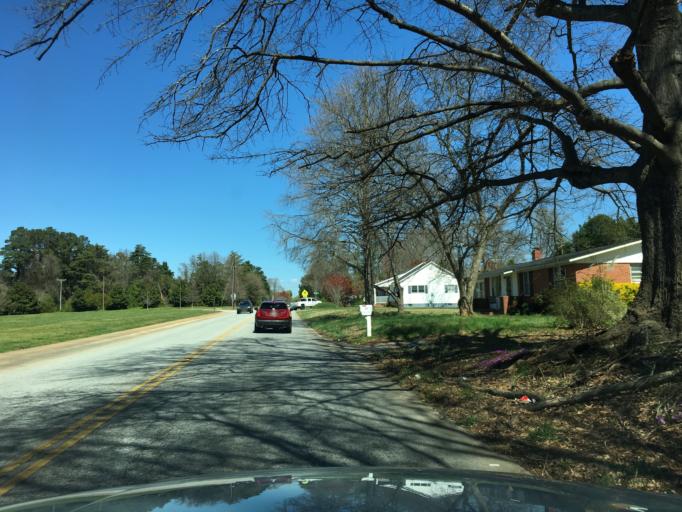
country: US
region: South Carolina
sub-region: Spartanburg County
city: Fairforest
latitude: 34.9257
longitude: -82.0014
